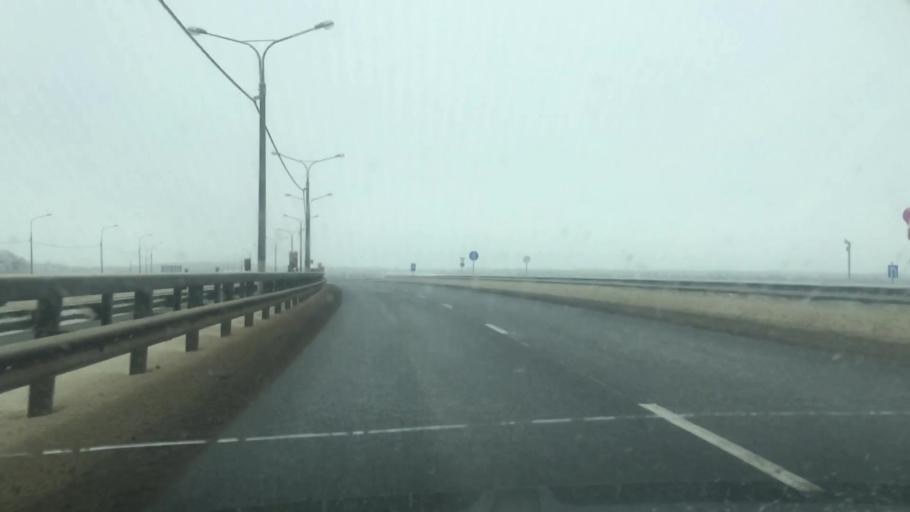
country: RU
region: Lipetsk
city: Yelets
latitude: 52.5431
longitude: 38.7216
